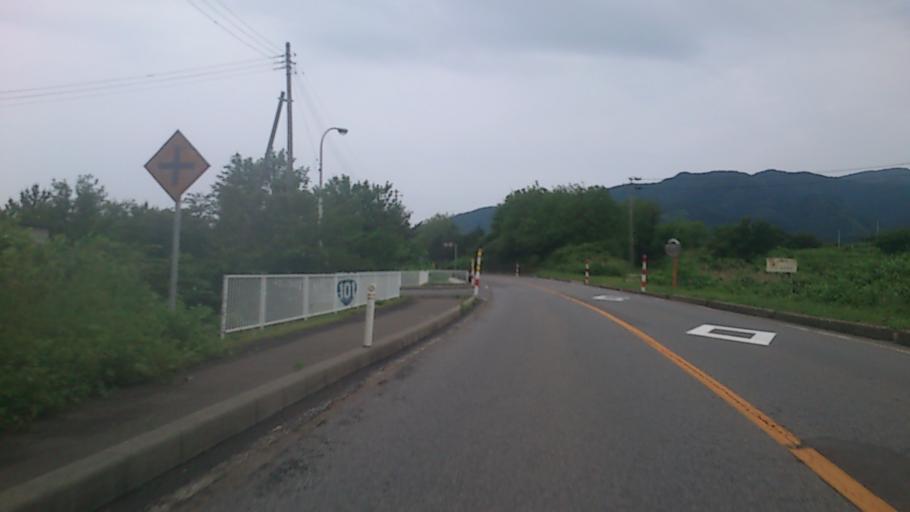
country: JP
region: Akita
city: Noshiromachi
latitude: 40.3638
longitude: 140.0214
